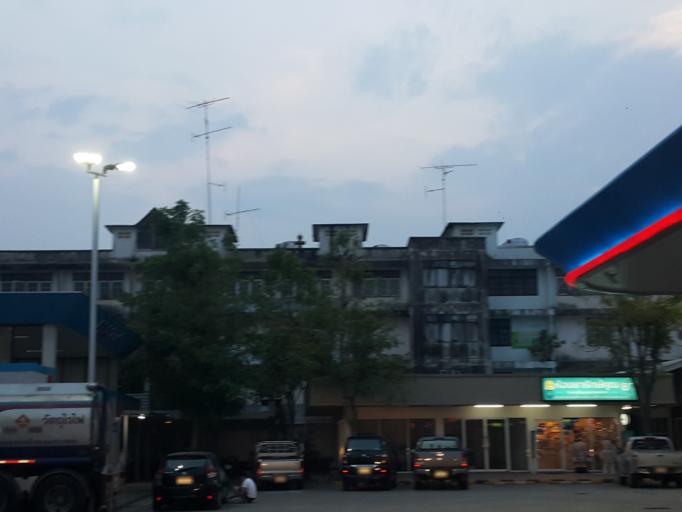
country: TH
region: Suphan Buri
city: Dan Chang
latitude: 14.8410
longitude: 99.6896
